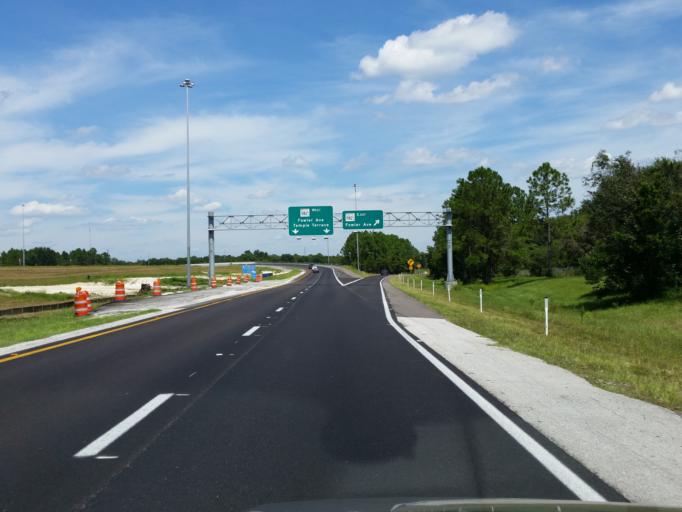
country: US
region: Florida
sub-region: Hillsborough County
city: Temple Terrace
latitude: 28.0503
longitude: -82.3514
